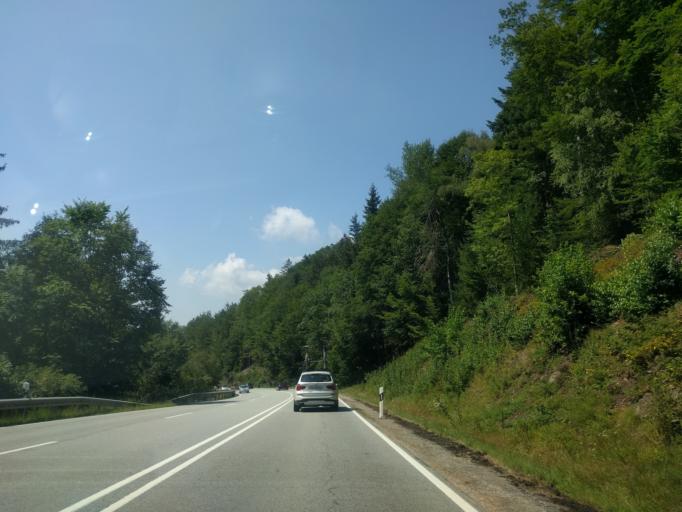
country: DE
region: Bavaria
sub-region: Lower Bavaria
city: Hunding
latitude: 48.8503
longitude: 13.2028
